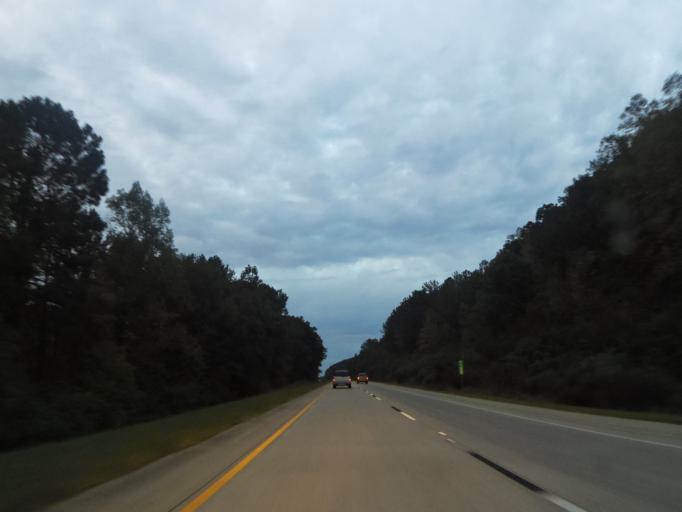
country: US
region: Alabama
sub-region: Etowah County
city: Gadsden
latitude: 34.0840
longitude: -86.0169
